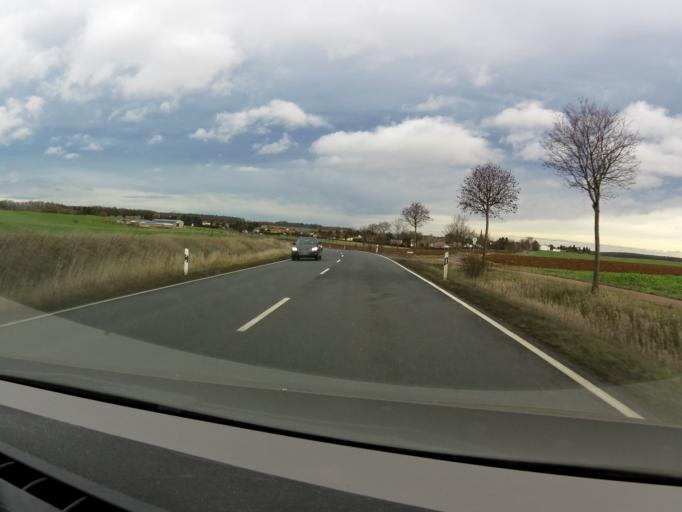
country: DE
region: Saxony-Anhalt
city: Blankenheim
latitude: 51.5441
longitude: 11.3955
